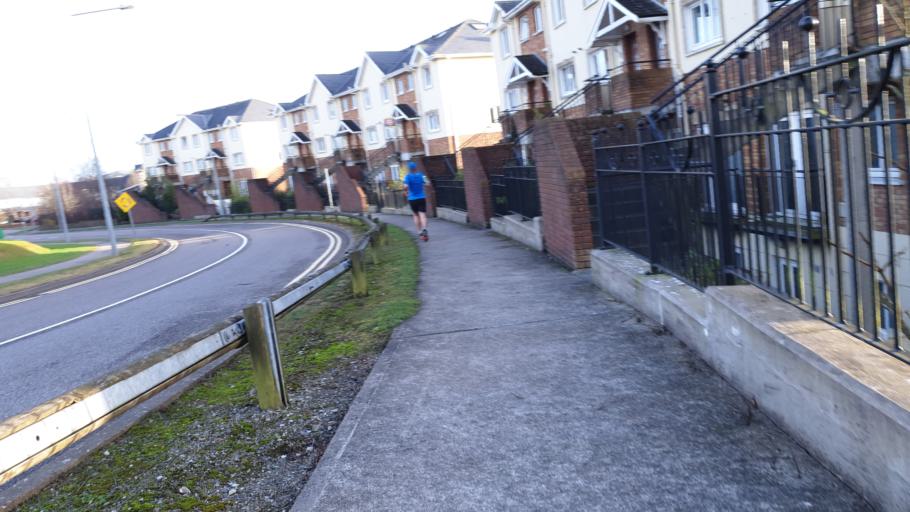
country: IE
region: Munster
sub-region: County Cork
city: Passage West
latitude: 51.8824
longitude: -8.3975
